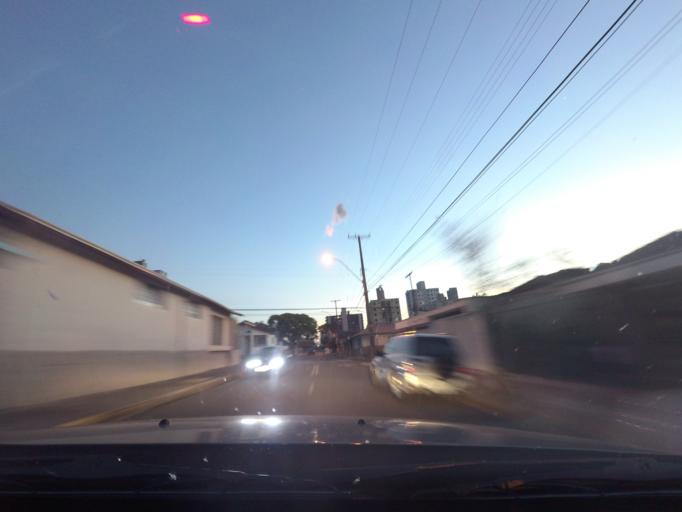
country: BR
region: Sao Paulo
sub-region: Piracicaba
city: Piracicaba
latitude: -22.7179
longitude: -47.6348
